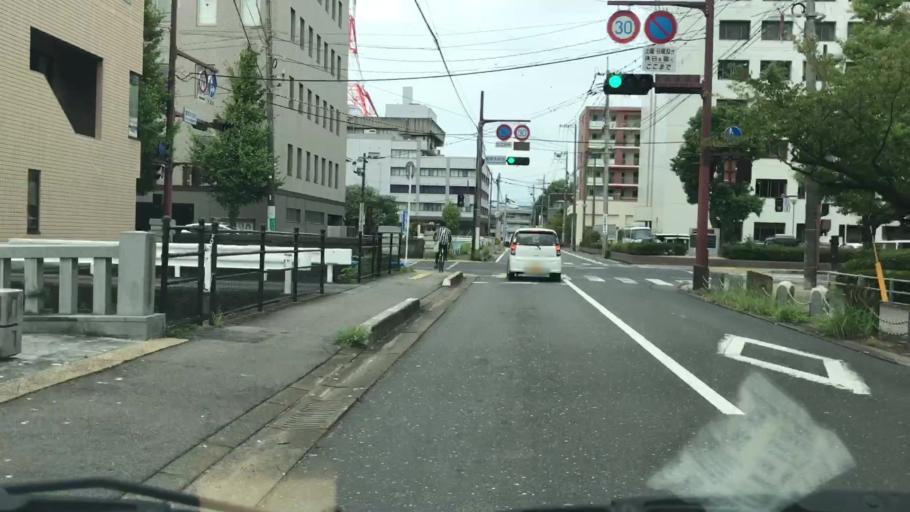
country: JP
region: Saga Prefecture
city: Saga-shi
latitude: 33.2501
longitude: 130.2976
